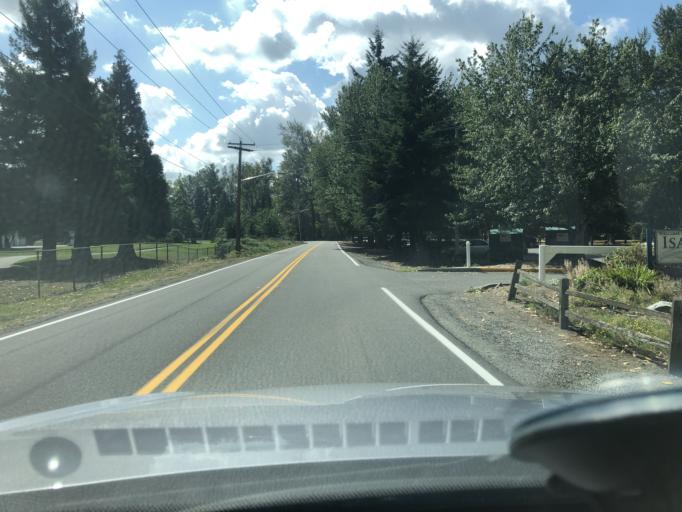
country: US
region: Washington
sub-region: King County
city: Lea Hill
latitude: 47.3341
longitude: -122.2102
